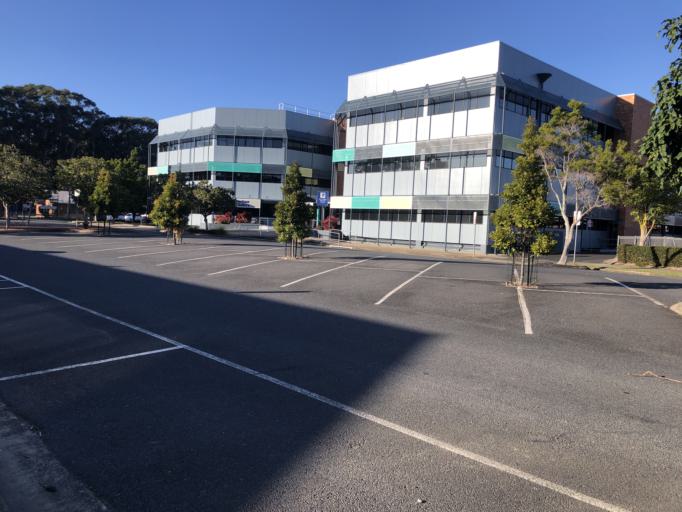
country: AU
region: New South Wales
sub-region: Coffs Harbour
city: Coffs Harbour
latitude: -30.2958
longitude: 153.1191
